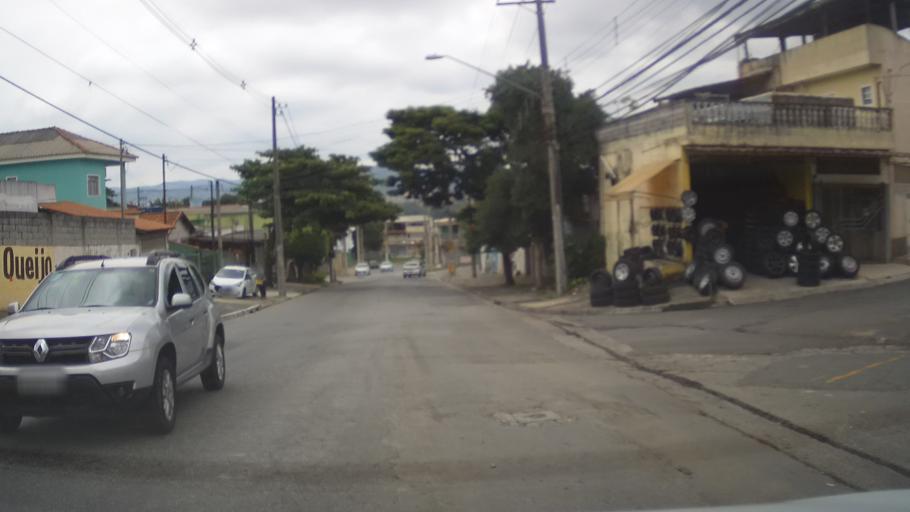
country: BR
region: Sao Paulo
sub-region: Itaquaquecetuba
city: Itaquaquecetuba
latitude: -23.4328
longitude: -46.4345
